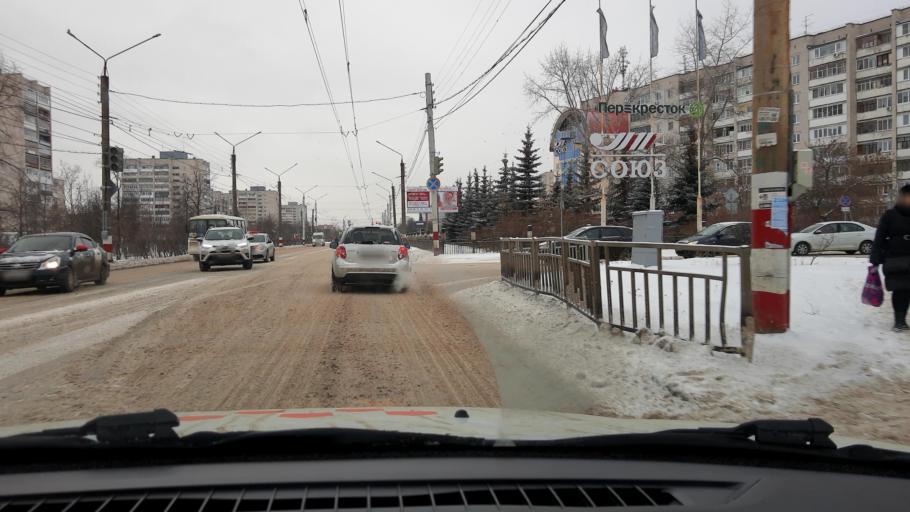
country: RU
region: Nizjnij Novgorod
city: Dzerzhinsk
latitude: 56.2268
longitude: 43.4043
